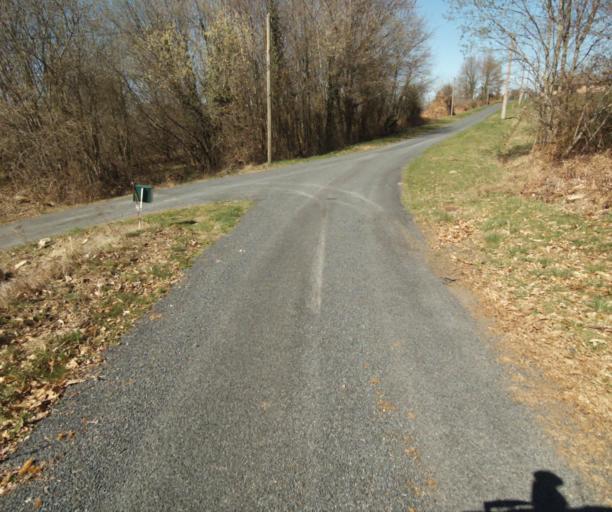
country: FR
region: Limousin
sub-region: Departement de la Correze
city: Saint-Mexant
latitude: 45.2762
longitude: 1.6537
